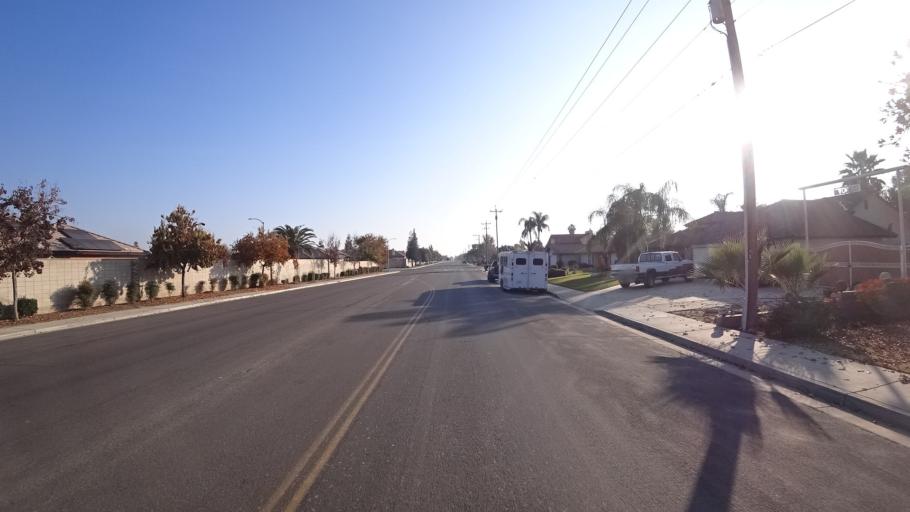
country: US
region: California
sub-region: Kern County
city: Rosedale
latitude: 35.3773
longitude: -119.1545
